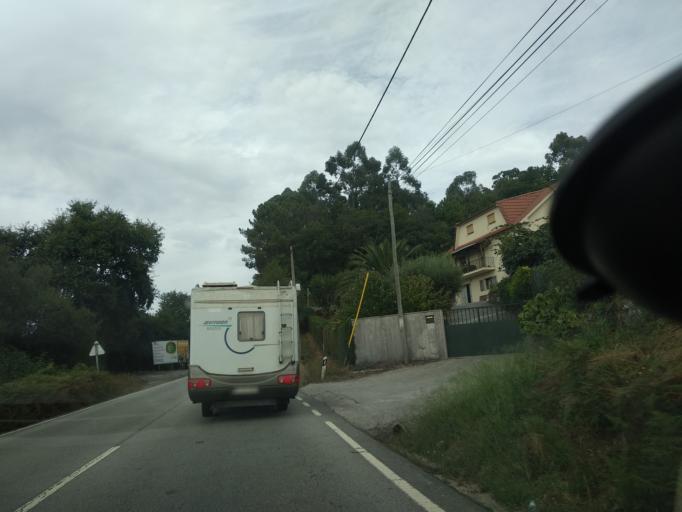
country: PT
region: Braga
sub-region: Vieira do Minho
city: Real
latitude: 41.6259
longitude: -8.2046
